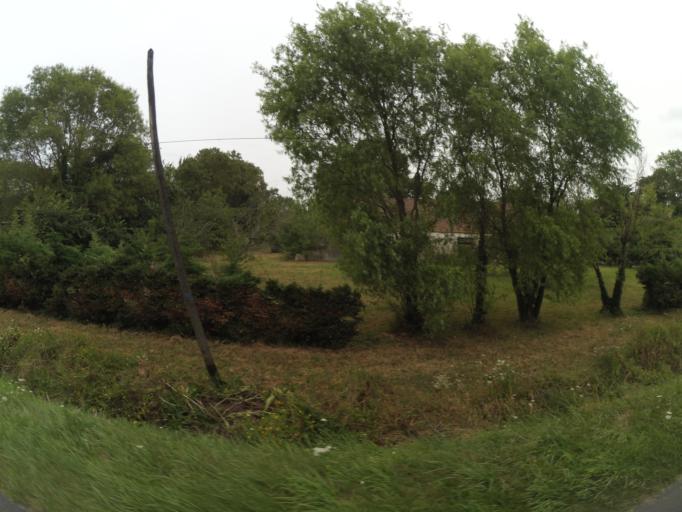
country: FR
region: Pays de la Loire
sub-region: Departement de la Vendee
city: Sallertaine
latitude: 46.8659
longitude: -1.9257
